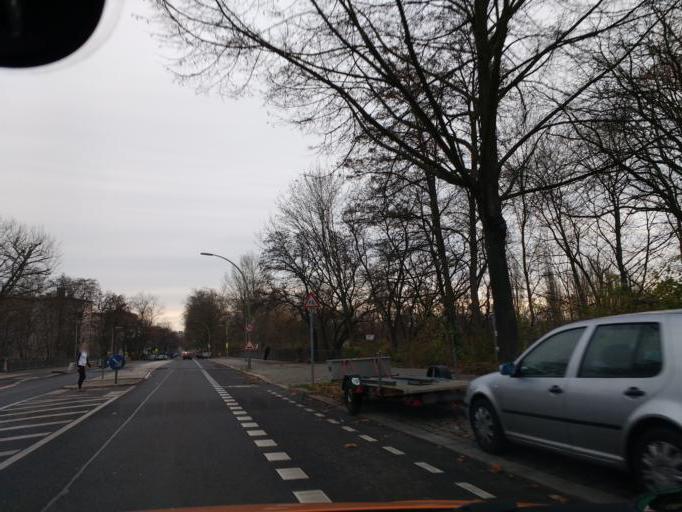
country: DE
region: Berlin
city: Mariendorf
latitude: 52.4465
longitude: 13.3649
